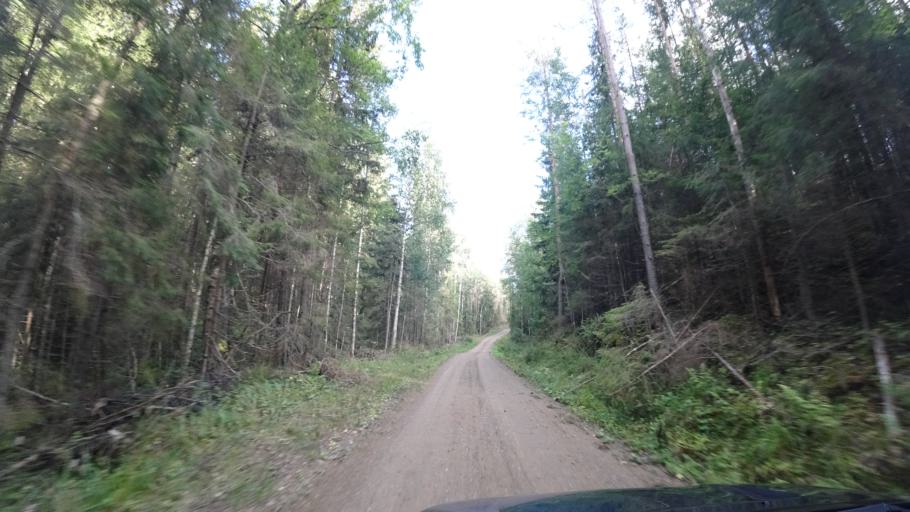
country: FI
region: Paijanne Tavastia
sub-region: Lahti
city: Auttoinen
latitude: 61.2243
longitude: 25.1958
